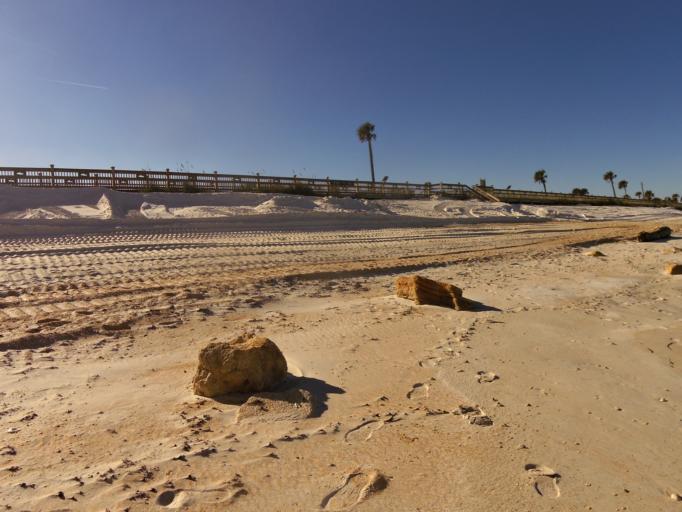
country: US
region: Florida
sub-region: Flagler County
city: Palm Coast
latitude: 29.6659
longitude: -81.2112
